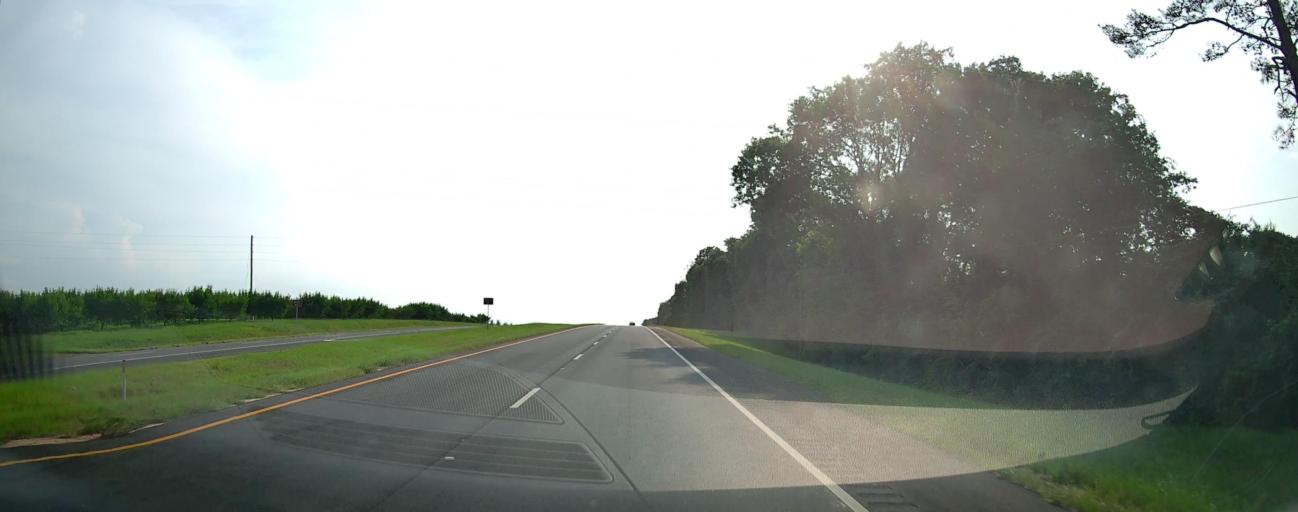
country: US
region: Georgia
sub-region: Taylor County
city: Butler
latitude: 32.5566
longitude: -84.1887
